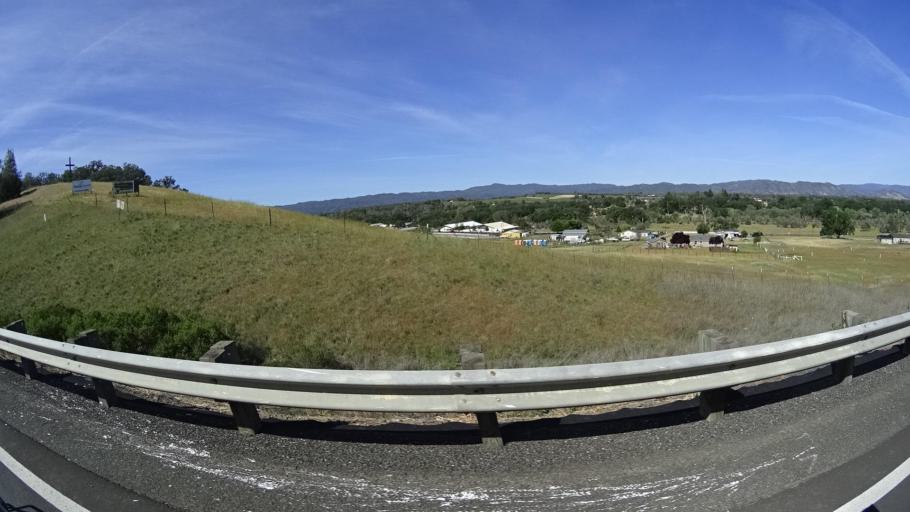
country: US
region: California
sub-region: Lake County
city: Kelseyville
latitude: 38.9628
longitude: -122.8289
